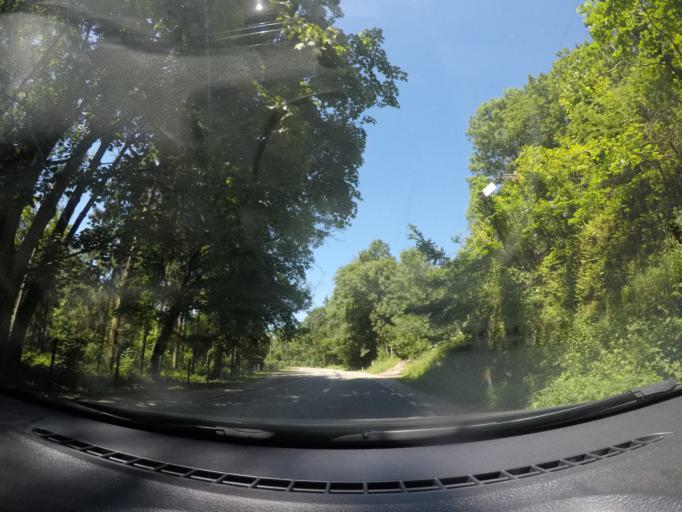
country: BE
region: Wallonia
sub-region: Province du Luxembourg
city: Wellin
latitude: 50.0599
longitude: 5.1420
